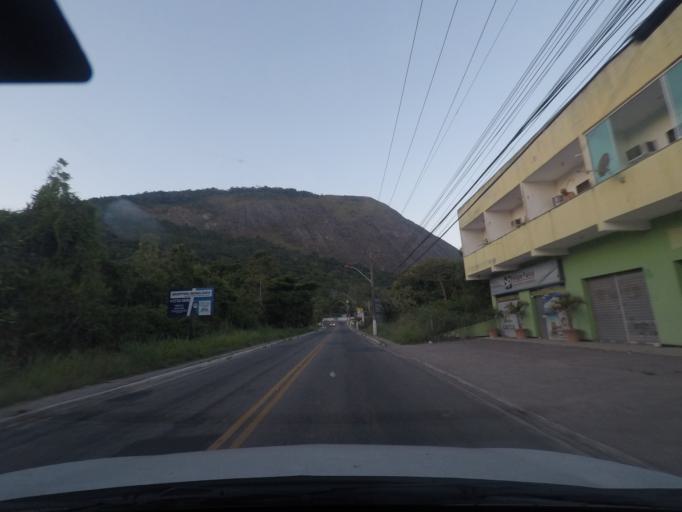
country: BR
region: Rio de Janeiro
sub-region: Marica
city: Marica
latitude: -22.9465
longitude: -42.9623
